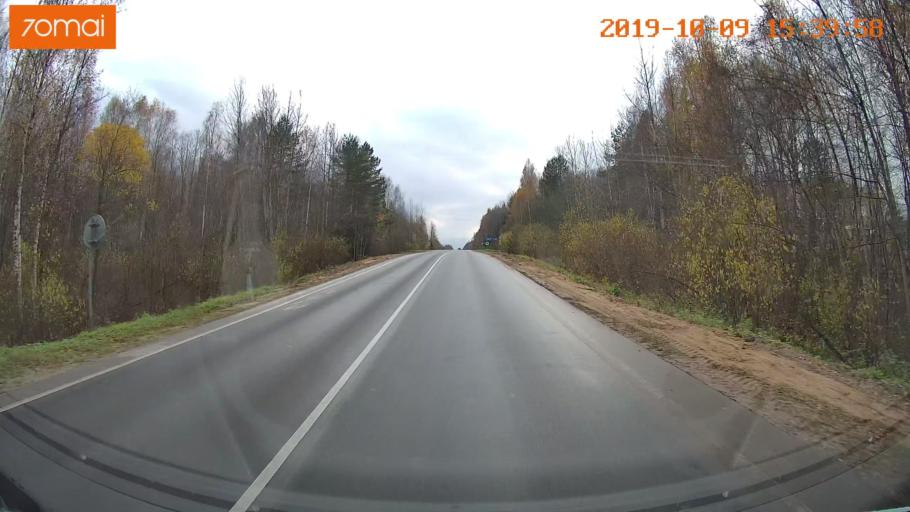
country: RU
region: Kostroma
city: Oktyabr'skiy
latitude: 57.8921
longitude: 41.1540
